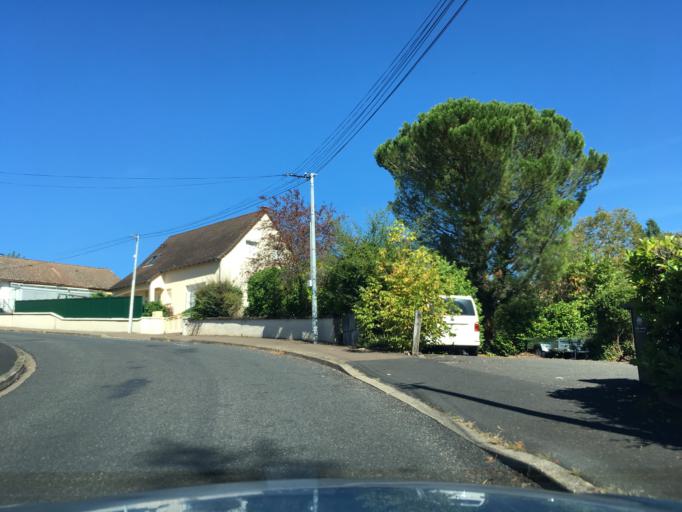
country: FR
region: Limousin
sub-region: Departement de la Correze
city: Brive-la-Gaillarde
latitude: 45.1675
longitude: 1.5197
